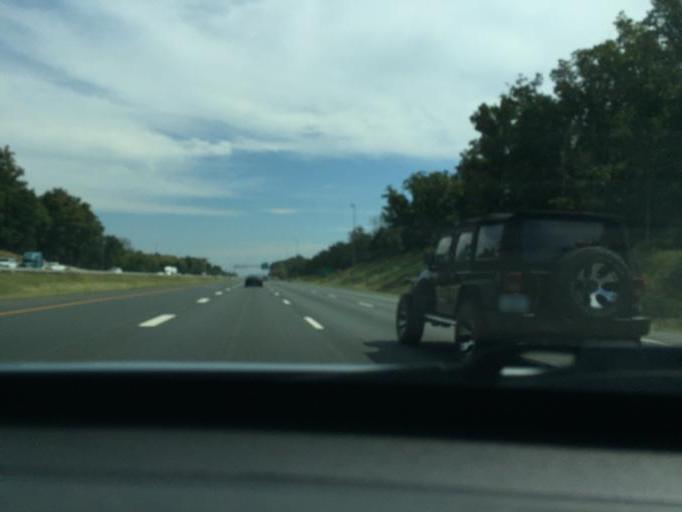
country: US
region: Virginia
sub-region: Prince William County
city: Bull Run
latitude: 38.7996
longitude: -77.5451
